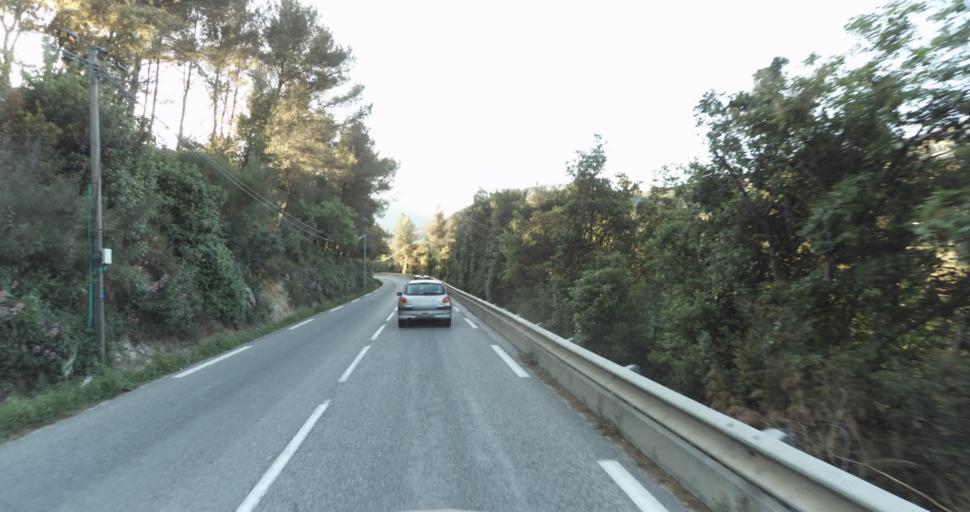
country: FR
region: Provence-Alpes-Cote d'Azur
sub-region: Departement du Var
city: La Valette-du-Var
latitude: 43.1566
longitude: 5.9595
